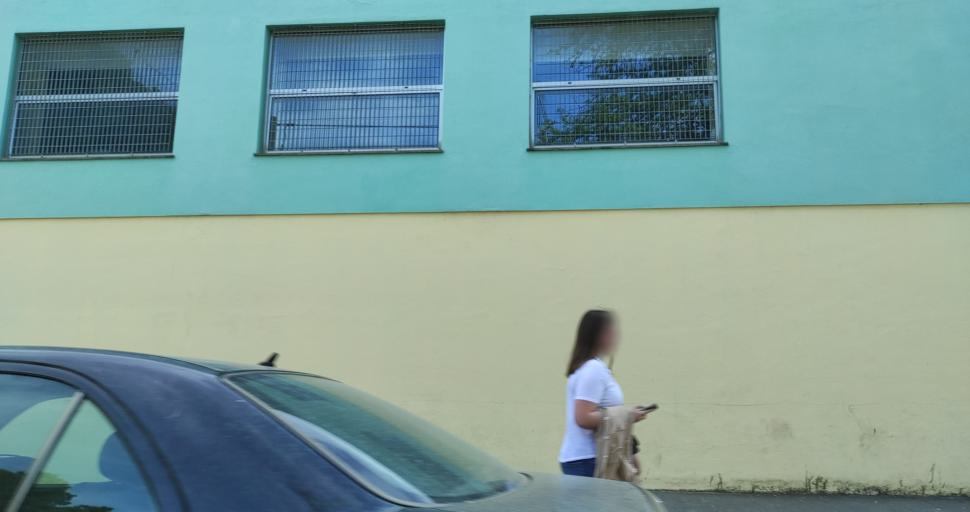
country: AL
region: Shkoder
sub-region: Rrethi i Shkodres
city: Shkoder
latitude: 42.0635
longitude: 19.5136
